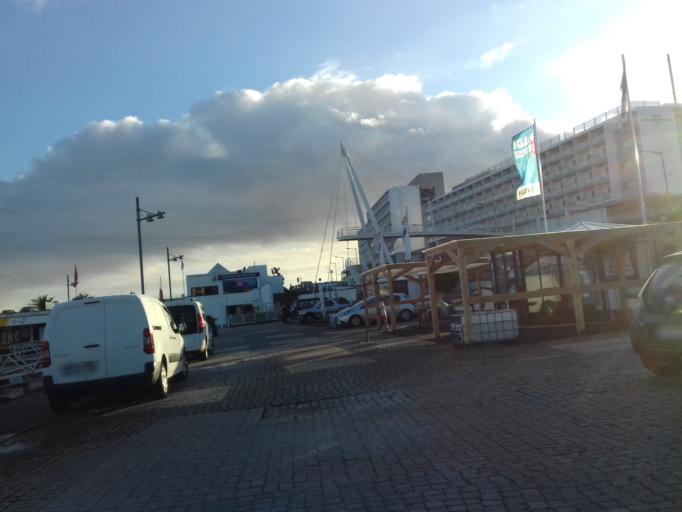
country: PT
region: Azores
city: Ponta Delgada
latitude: 37.7413
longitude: -25.6593
